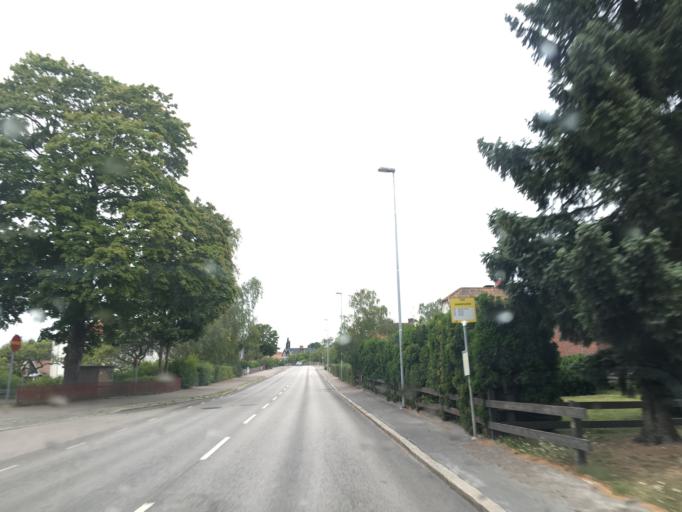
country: SE
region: Kalmar
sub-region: Nybro Kommun
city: Nybro
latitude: 56.7394
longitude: 15.9219
